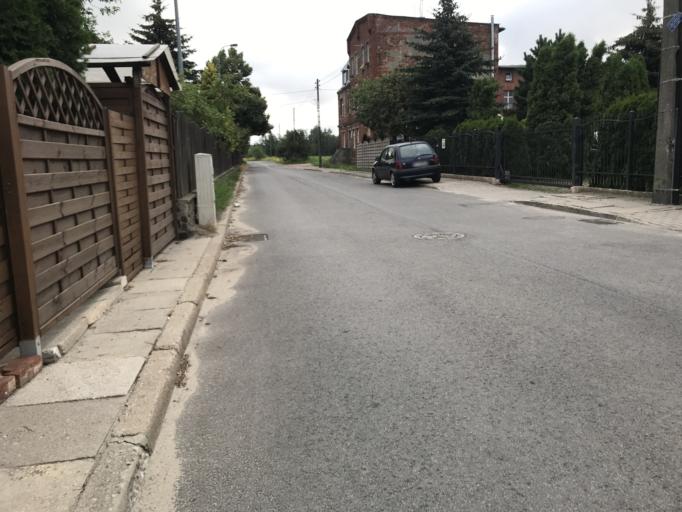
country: PL
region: Pomeranian Voivodeship
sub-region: Gdansk
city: Gdansk
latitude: 54.3364
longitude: 18.6784
